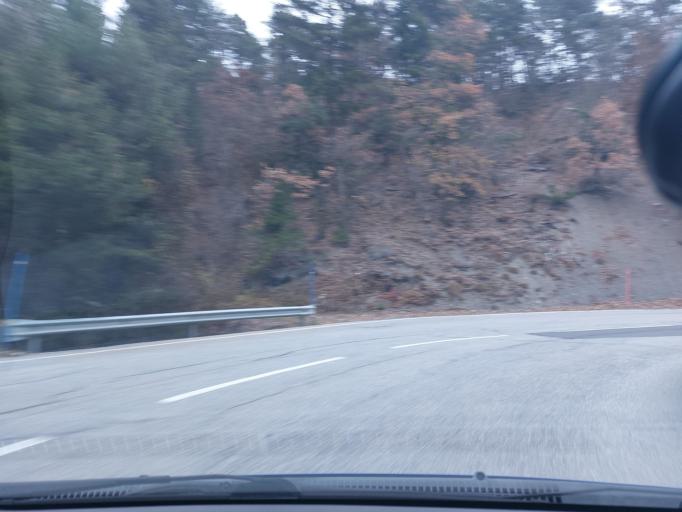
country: CH
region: Valais
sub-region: Herens District
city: Ayent
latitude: 46.2931
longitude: 7.4271
